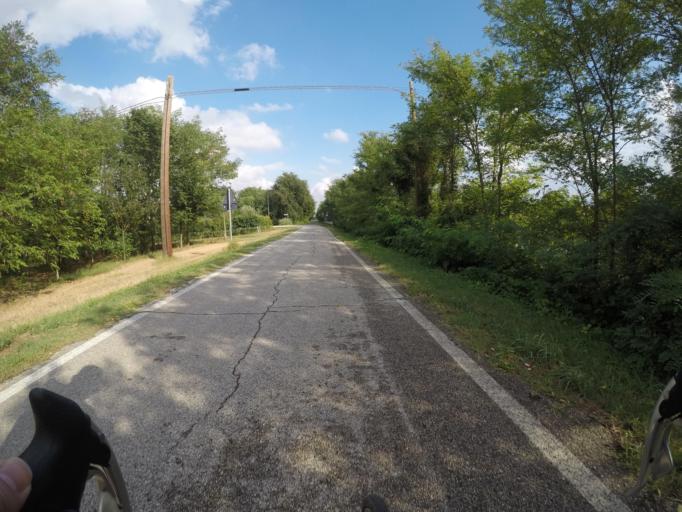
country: IT
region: Veneto
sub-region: Provincia di Rovigo
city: Frassinelle Polesine
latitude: 44.9973
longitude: 11.6999
